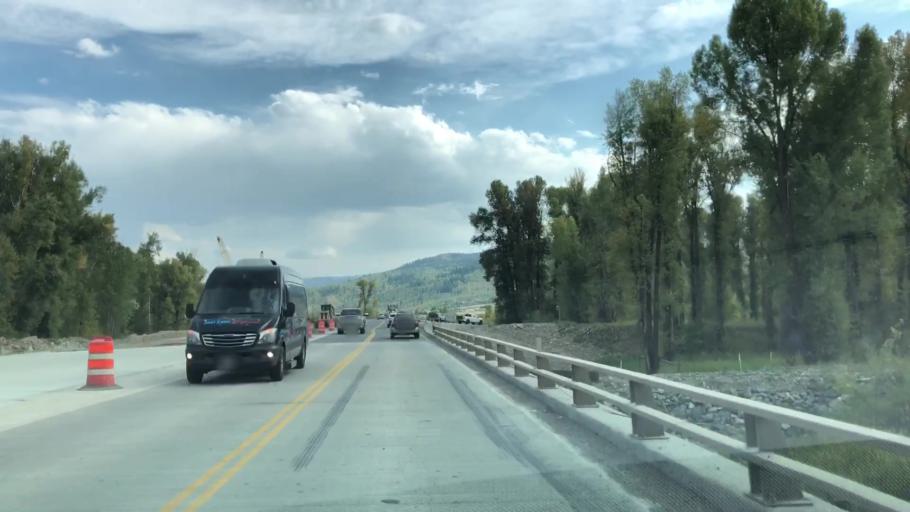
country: US
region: Wyoming
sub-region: Teton County
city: South Park
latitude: 43.3889
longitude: -110.7470
